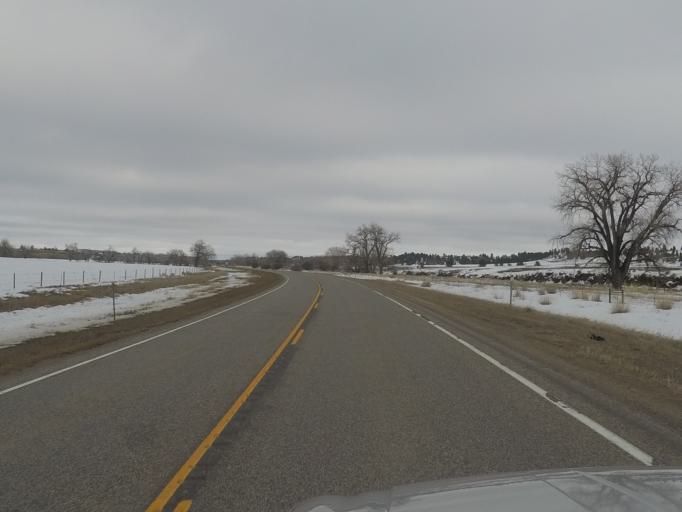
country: US
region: Montana
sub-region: Golden Valley County
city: Ryegate
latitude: 46.3009
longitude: -109.1085
